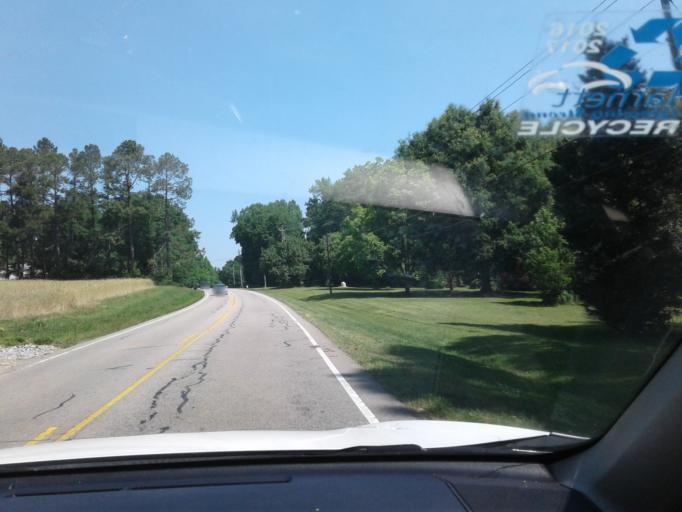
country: US
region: North Carolina
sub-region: Wake County
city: Holly Springs
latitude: 35.6109
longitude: -78.8403
